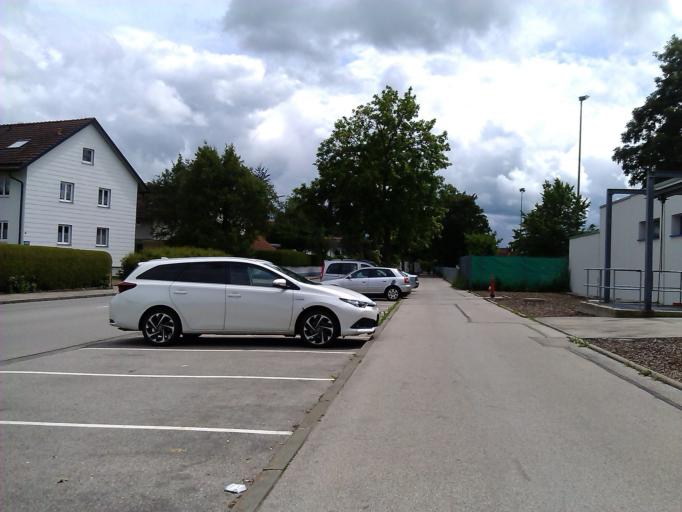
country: DE
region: Bavaria
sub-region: Swabia
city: Marktoberdorf
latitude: 47.7725
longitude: 10.6150
